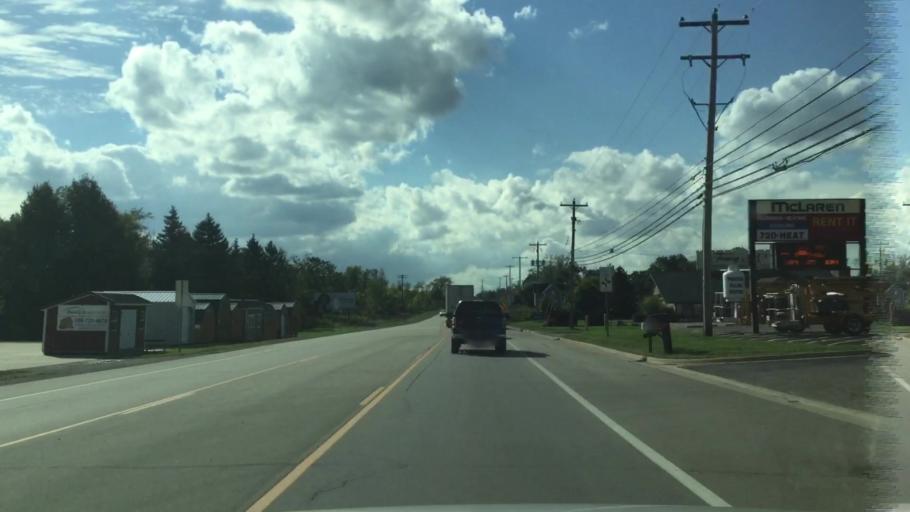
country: US
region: Michigan
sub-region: Shiawassee County
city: Owosso
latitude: 42.9975
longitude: -84.2096
